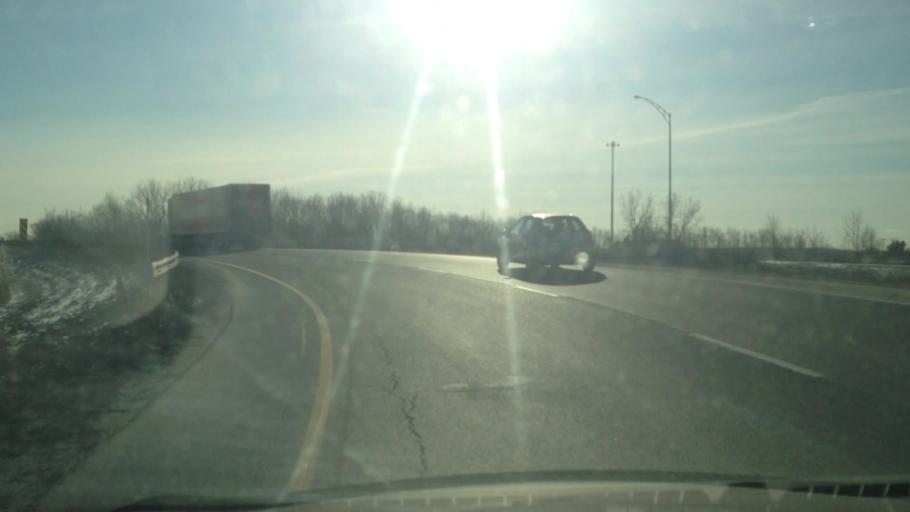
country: CA
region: Quebec
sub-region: Laurentides
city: Boisbriand
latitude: 45.6000
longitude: -73.8646
